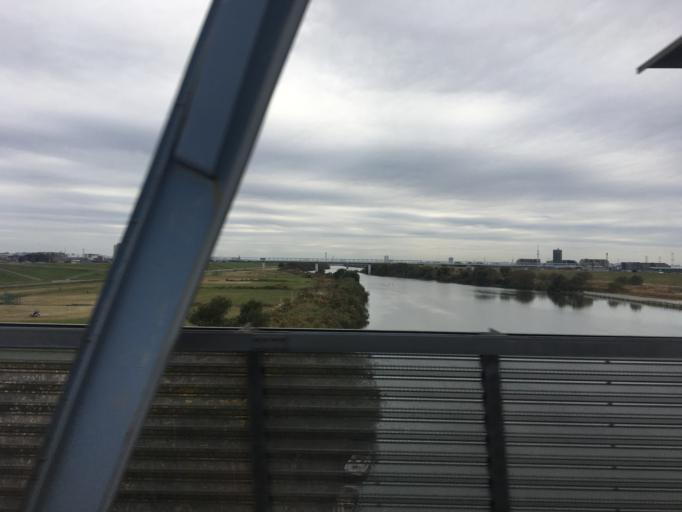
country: JP
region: Chiba
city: Nagareyama
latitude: 35.8445
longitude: 139.8906
